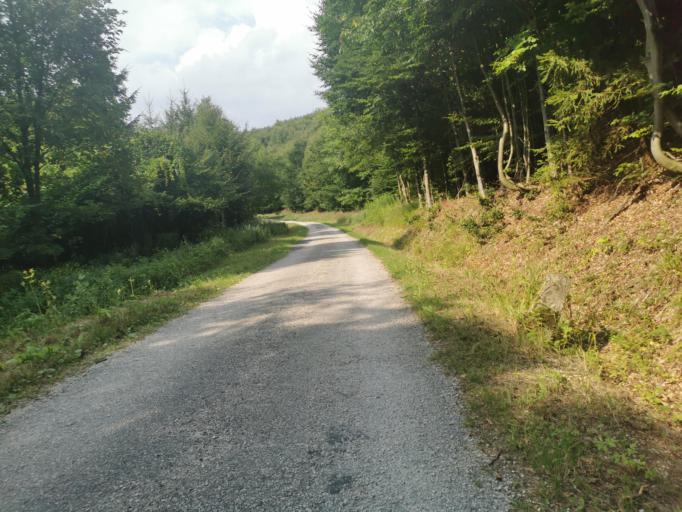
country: SK
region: Nitriansky
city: Stara Tura
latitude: 48.8209
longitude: 17.6316
